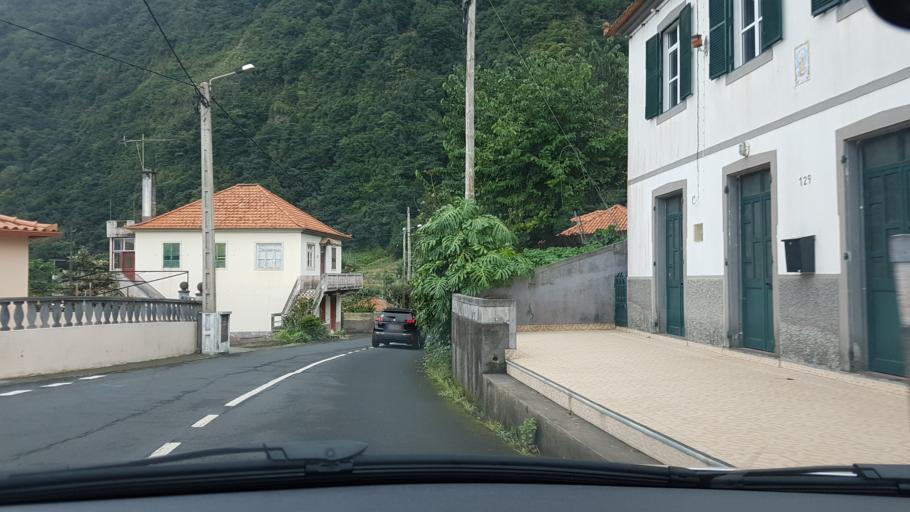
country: PT
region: Madeira
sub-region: Santana
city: Santana
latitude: 32.8246
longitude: -16.9562
